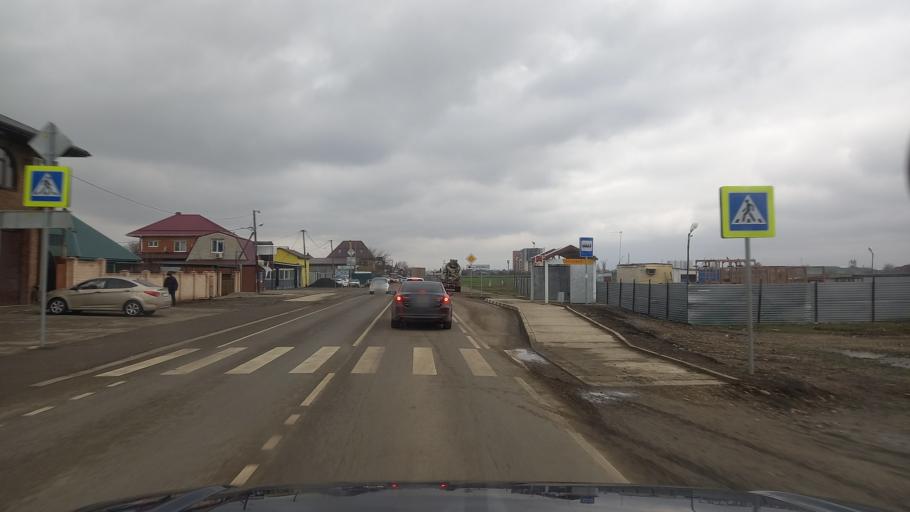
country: RU
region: Krasnodarskiy
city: Pashkovskiy
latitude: 45.0591
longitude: 39.1607
